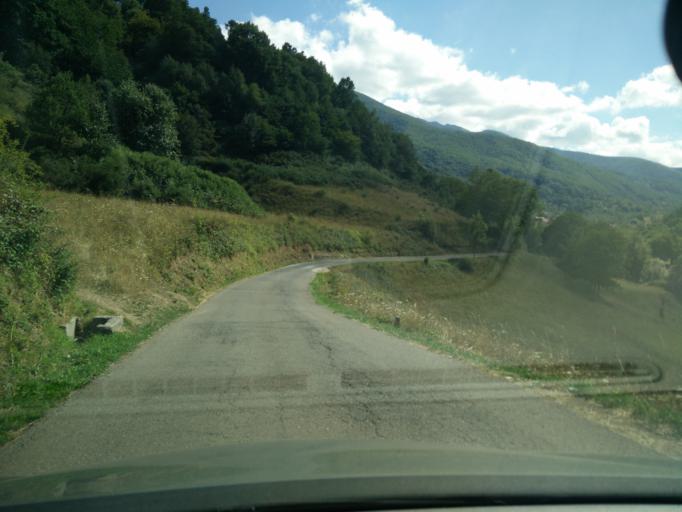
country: ES
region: Castille and Leon
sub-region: Provincia de Leon
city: Posada de Valdeon
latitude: 43.1590
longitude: -4.9116
